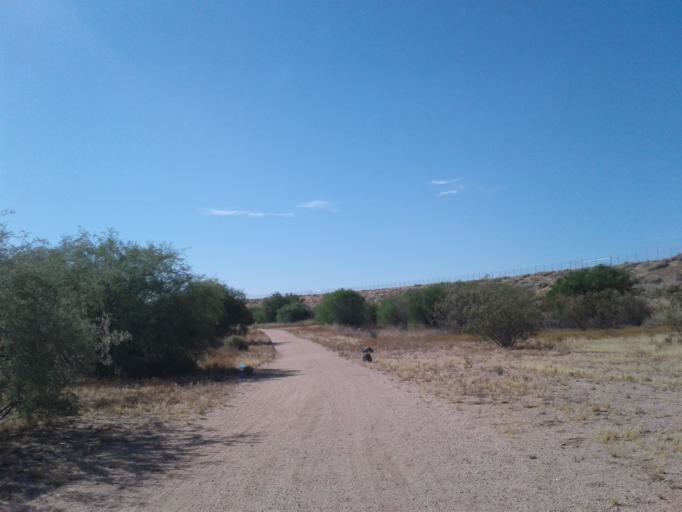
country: US
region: Arizona
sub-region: Maricopa County
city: Cave Creek
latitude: 33.6819
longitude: -112.0295
